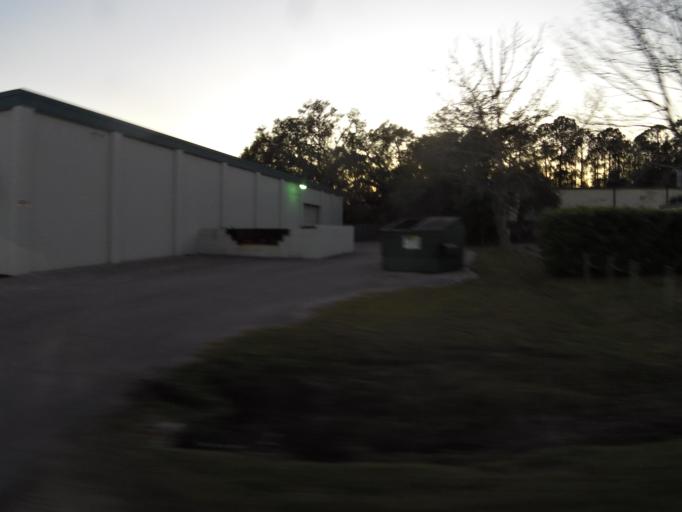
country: US
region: Florida
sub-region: Duval County
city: Jacksonville
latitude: 30.2715
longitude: -81.6307
